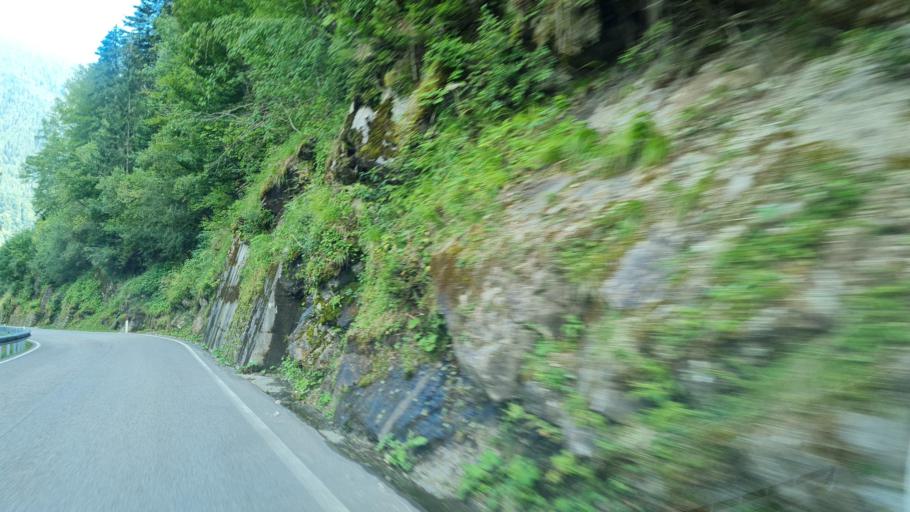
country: IT
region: Trentino-Alto Adige
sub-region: Provincia di Trento
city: Carzano
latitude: 46.1189
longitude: 11.4859
